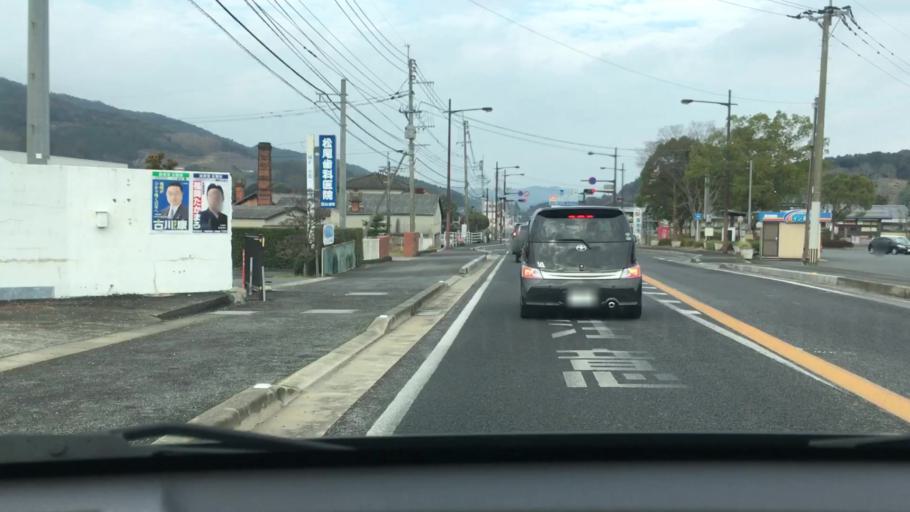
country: JP
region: Saga Prefecture
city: Imaricho-ko
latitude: 33.3124
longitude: 129.9285
